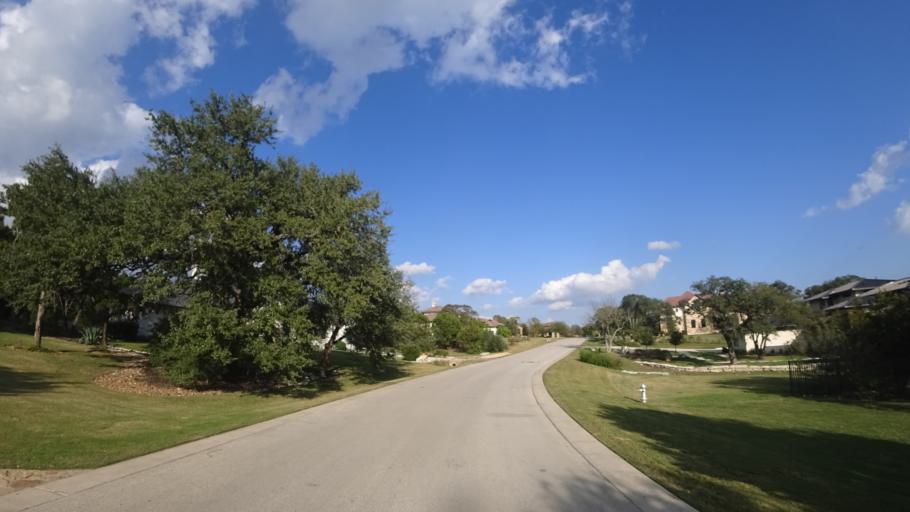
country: US
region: Texas
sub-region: Travis County
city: Barton Creek
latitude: 30.2785
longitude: -97.8785
